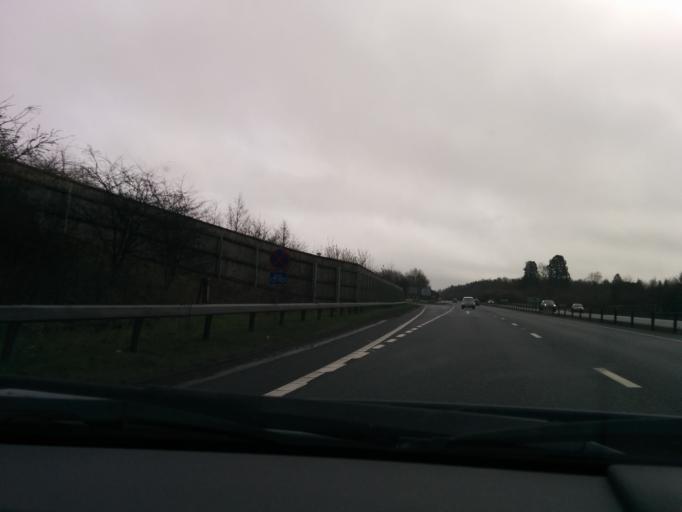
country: GB
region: England
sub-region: Hampshire
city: Highclere
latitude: 51.3646
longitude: -1.3606
